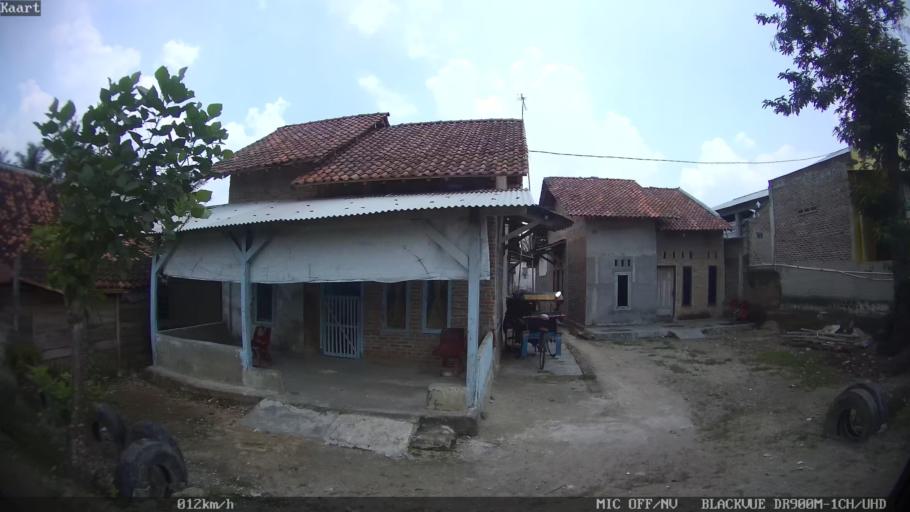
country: ID
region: Lampung
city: Pringsewu
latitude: -5.3429
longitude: 104.9811
